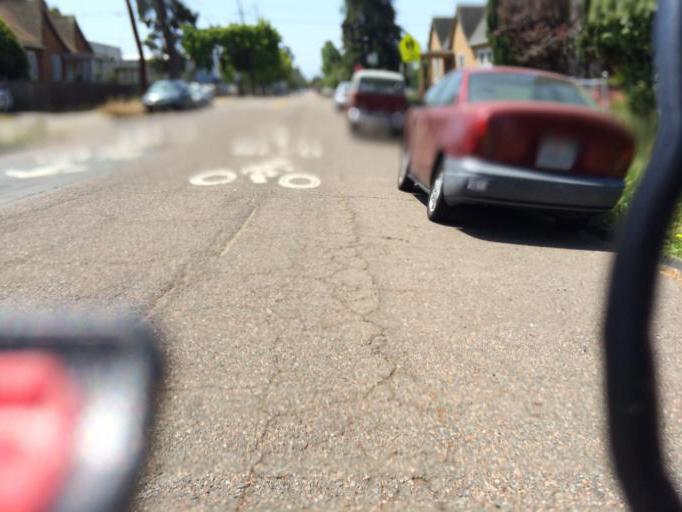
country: US
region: California
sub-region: Alameda County
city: Berkeley
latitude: 37.8615
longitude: -122.2696
